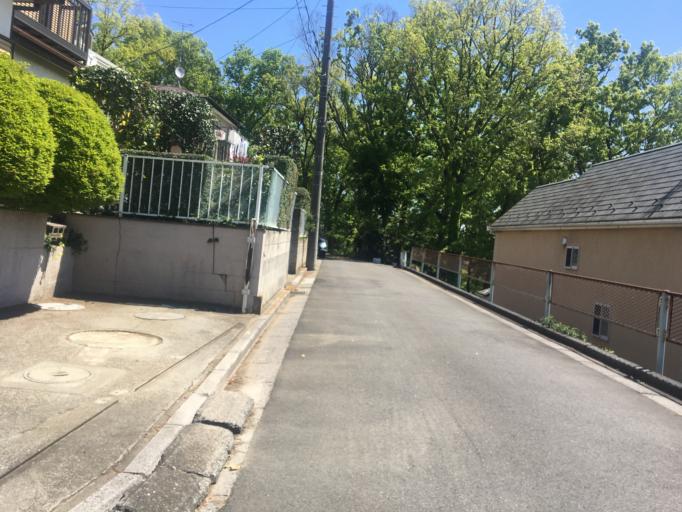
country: JP
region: Saitama
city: Shiki
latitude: 35.8374
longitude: 139.5620
